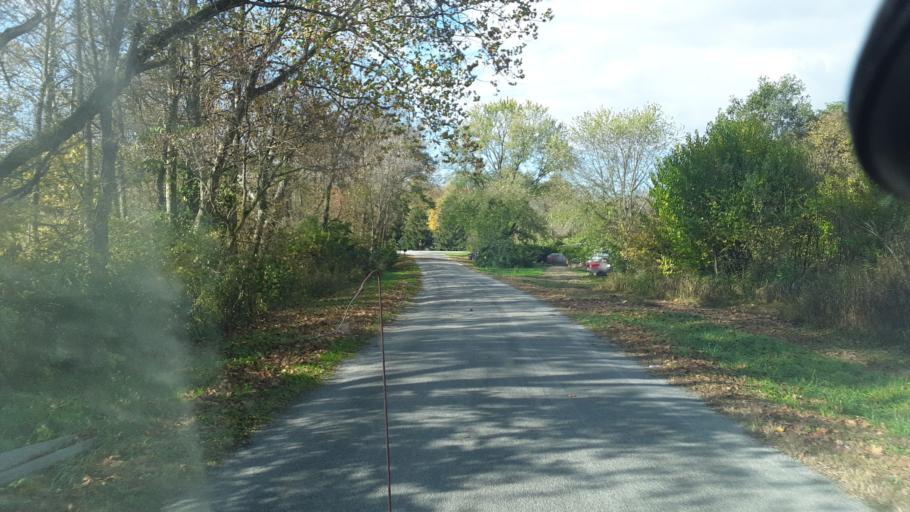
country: US
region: Ohio
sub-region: Highland County
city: Leesburg
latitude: 39.3055
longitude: -83.5200
